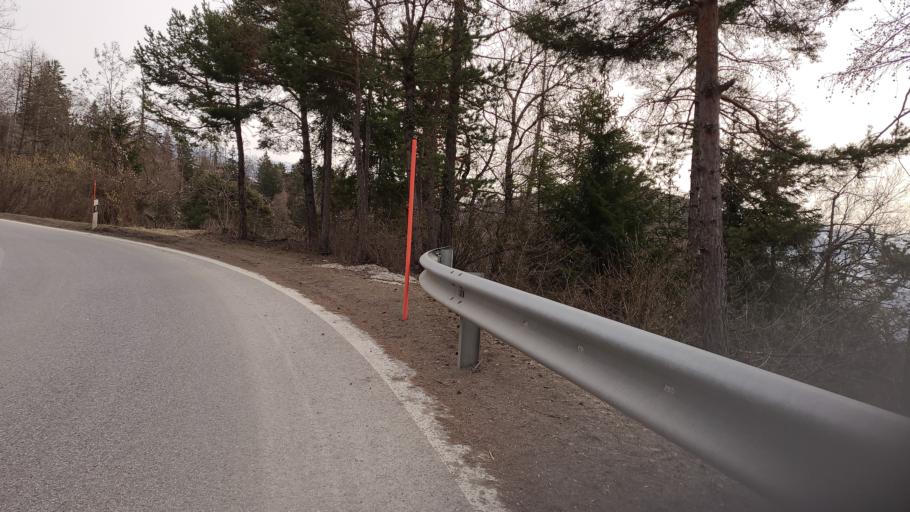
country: CH
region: Valais
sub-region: Sierre District
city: Lens
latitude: 46.2849
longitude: 7.4416
